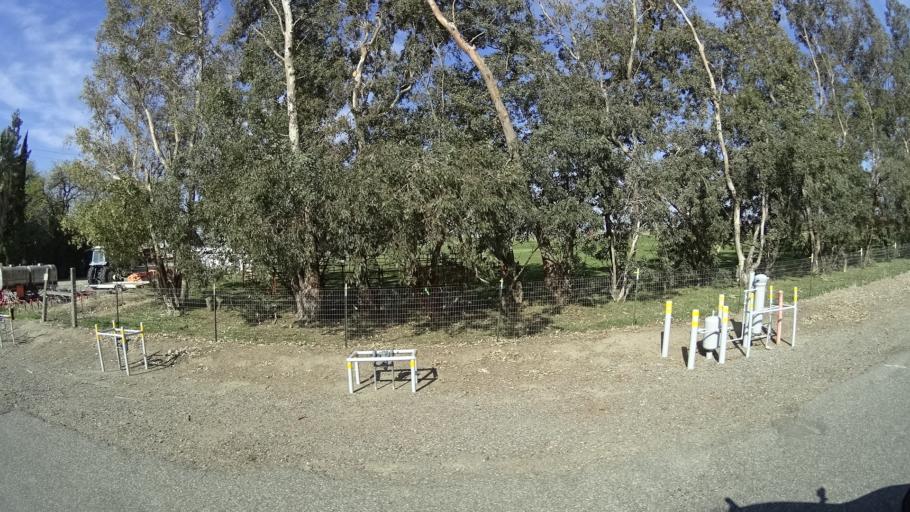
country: US
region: California
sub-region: Glenn County
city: Willows
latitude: 39.5718
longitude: -122.0464
